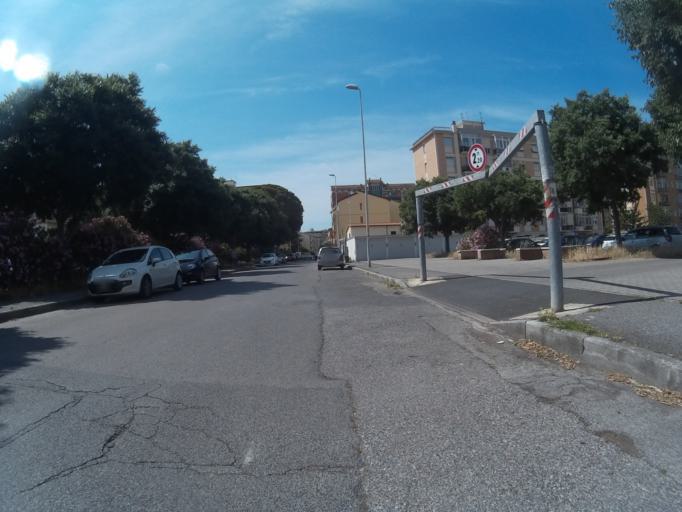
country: IT
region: Tuscany
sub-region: Provincia di Livorno
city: Livorno
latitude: 43.5469
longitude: 10.3259
